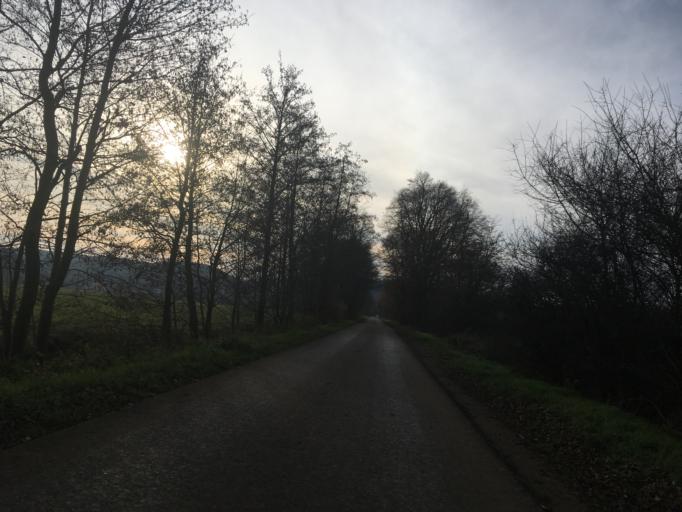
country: DE
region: Brandenburg
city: Falkenberg
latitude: 52.8112
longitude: 13.9665
